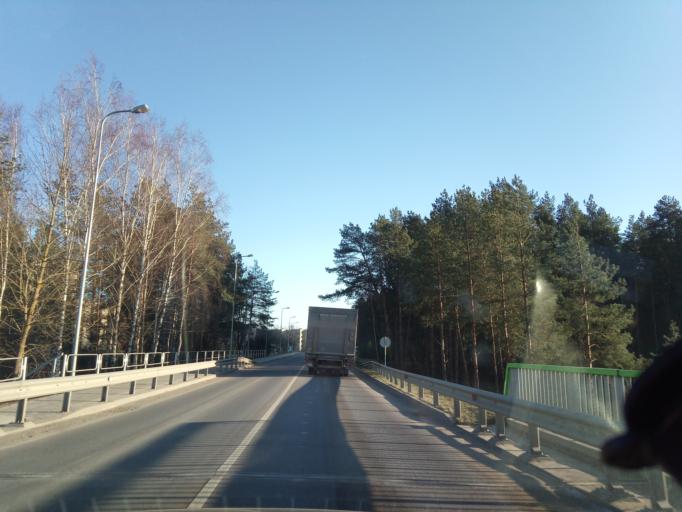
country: LT
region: Alytaus apskritis
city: Druskininkai
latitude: 54.0263
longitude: 23.9961
